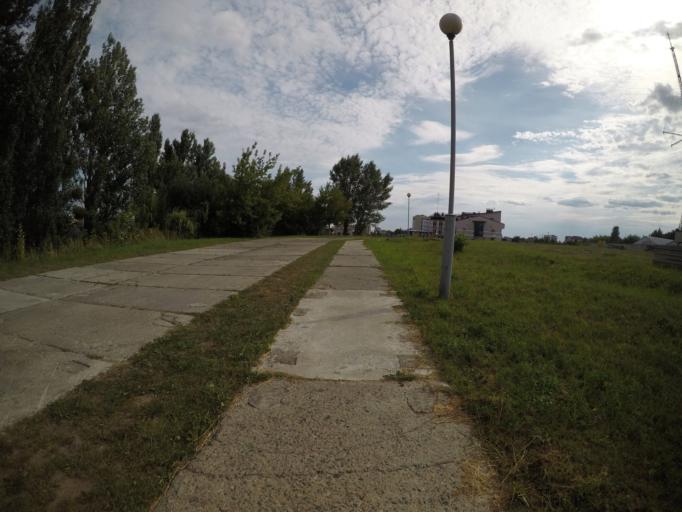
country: BY
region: Grodnenskaya
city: Hrodna
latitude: 53.7028
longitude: 23.8276
